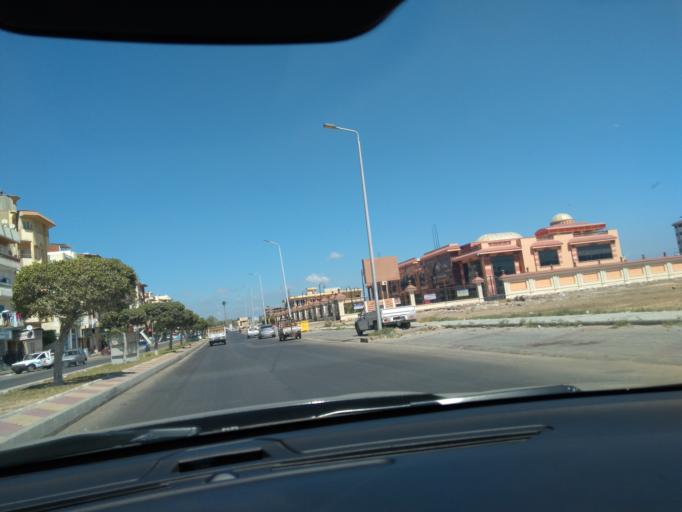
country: EG
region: Dumyat
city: Faraskur
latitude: 31.4276
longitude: 31.6885
